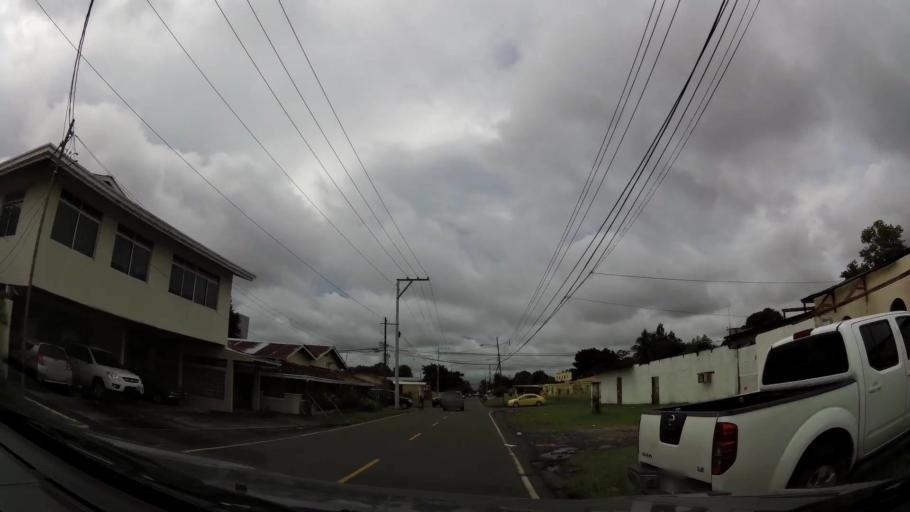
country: PA
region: Chiriqui
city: David
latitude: 8.4369
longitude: -82.4268
